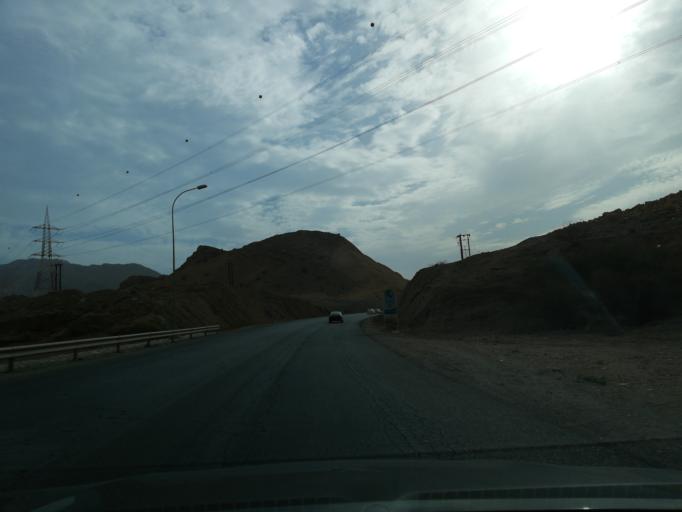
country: OM
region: Muhafazat Masqat
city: Bawshar
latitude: 23.4783
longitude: 58.3050
